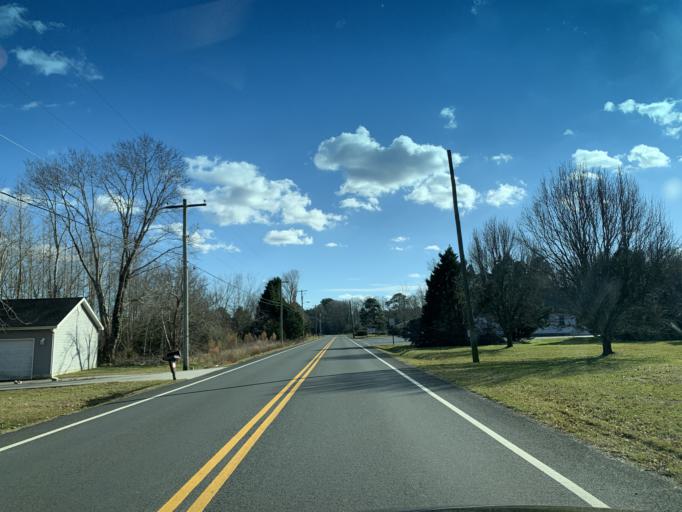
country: US
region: Maryland
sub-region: Worcester County
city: Berlin
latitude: 38.3641
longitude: -75.2013
